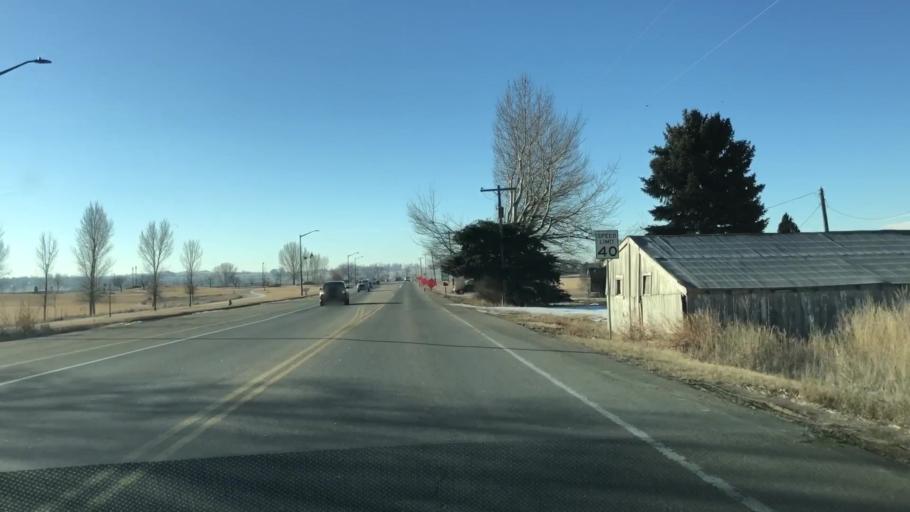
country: US
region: Colorado
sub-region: Larimer County
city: Loveland
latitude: 40.4037
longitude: -105.0212
